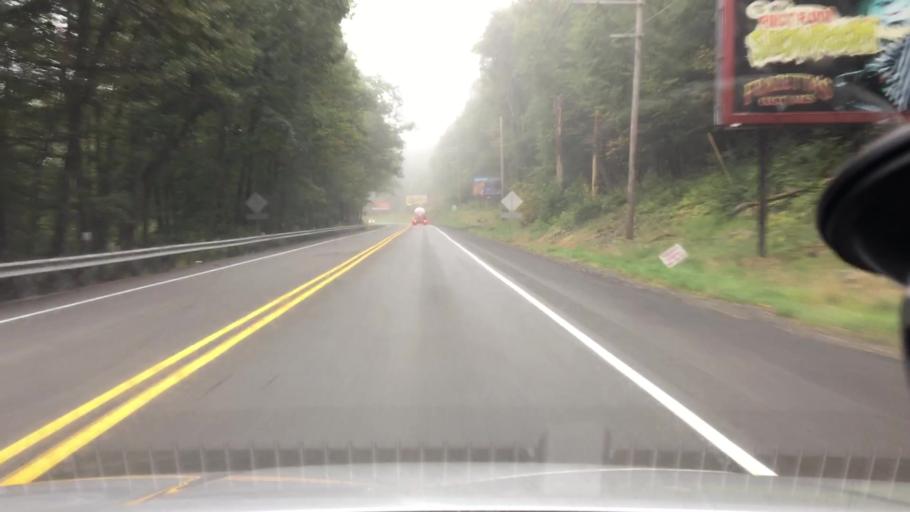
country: US
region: Pennsylvania
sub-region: Monroe County
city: Mount Pocono
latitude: 41.1257
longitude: -75.3506
